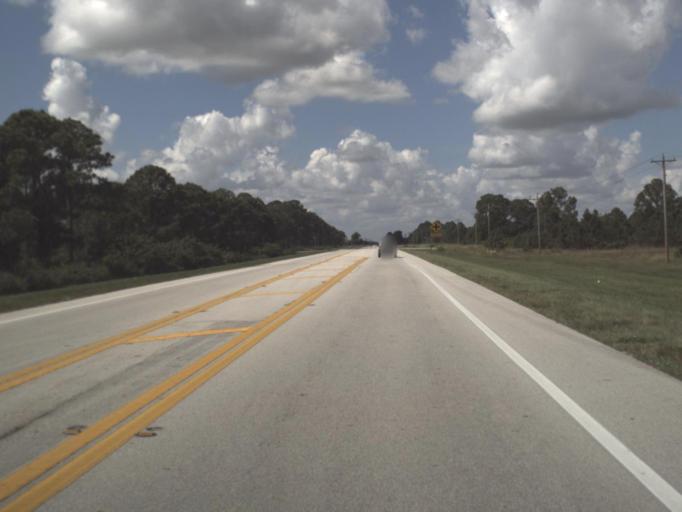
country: US
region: Florida
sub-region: Lee County
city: Lehigh Acres
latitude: 26.5201
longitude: -81.5703
